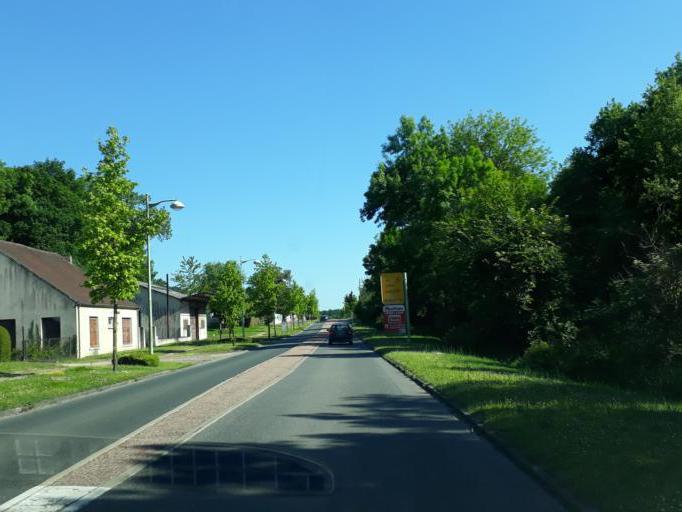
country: FR
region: Centre
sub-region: Departement du Cher
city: Lere
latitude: 47.4759
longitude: 2.9273
